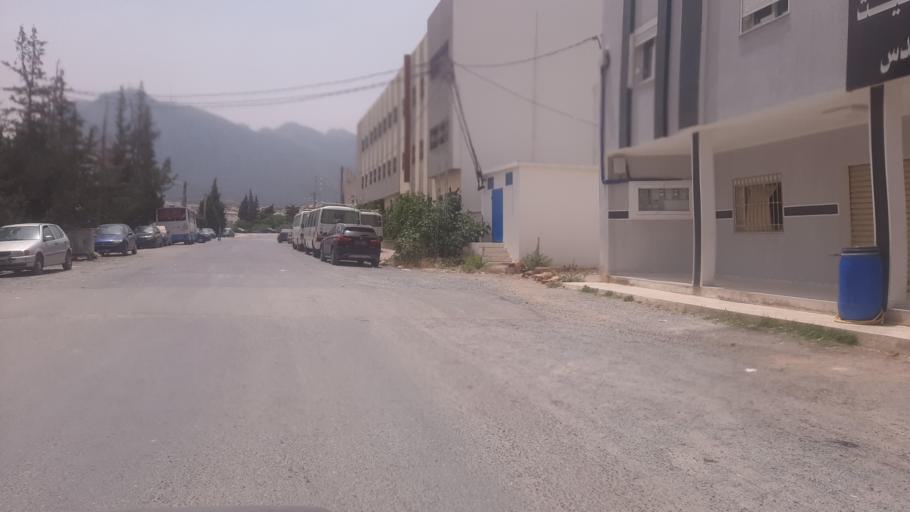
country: TN
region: Zaghwan
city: Zaghouan
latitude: 36.4146
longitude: 10.1356
